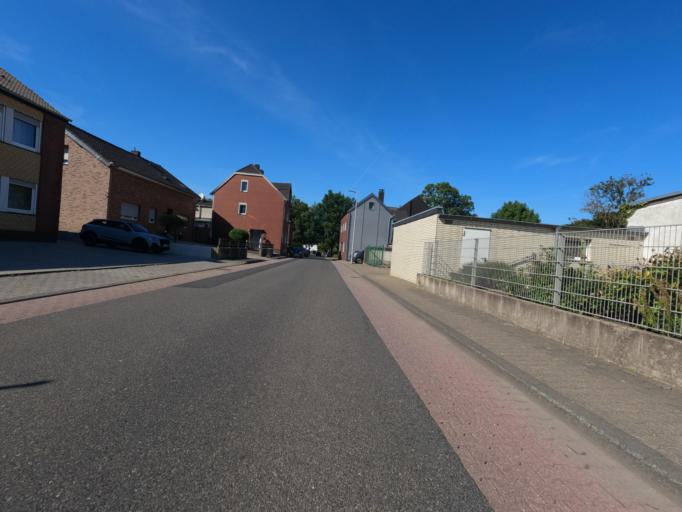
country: DE
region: North Rhine-Westphalia
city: Baesweiler
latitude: 50.8860
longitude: 6.2005
